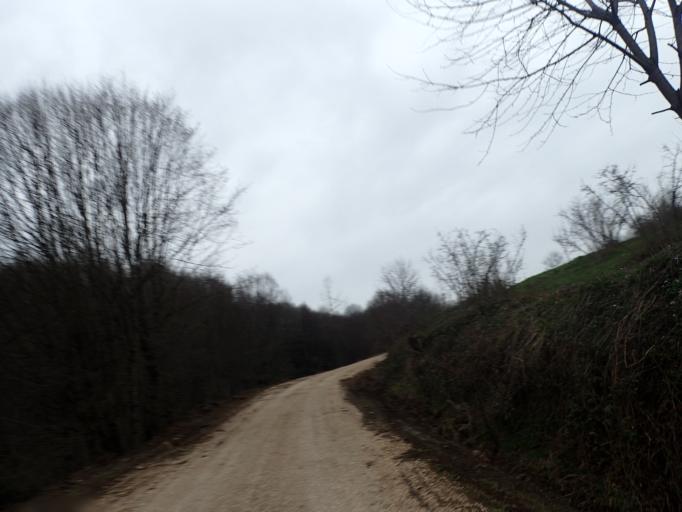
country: TR
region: Ordu
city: Kumru
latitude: 40.8101
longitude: 37.1670
